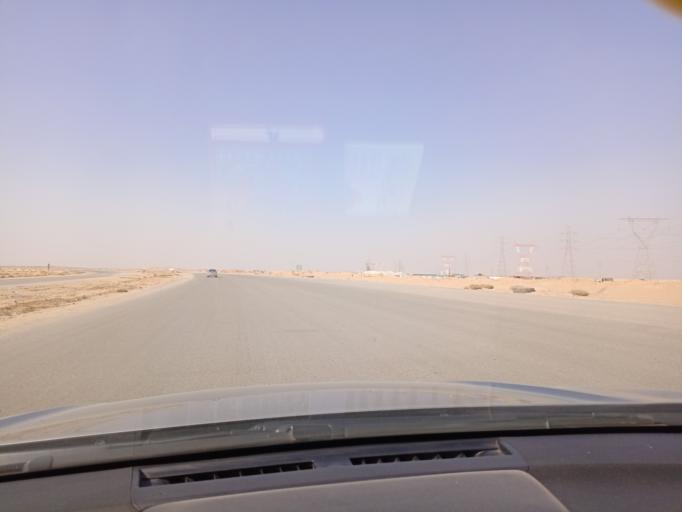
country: EG
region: Muhafazat al Qalyubiyah
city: Al Khankah
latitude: 30.0360
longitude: 31.7168
